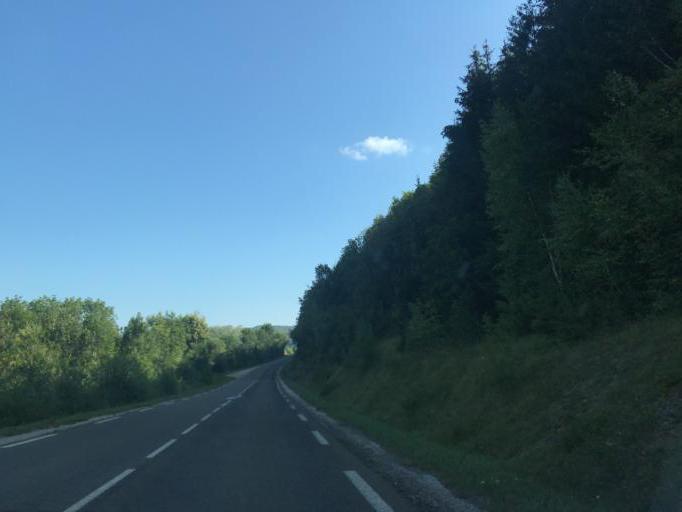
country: FR
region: Franche-Comte
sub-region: Departement du Jura
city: Moirans-en-Montagne
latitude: 46.4005
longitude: 5.7337
